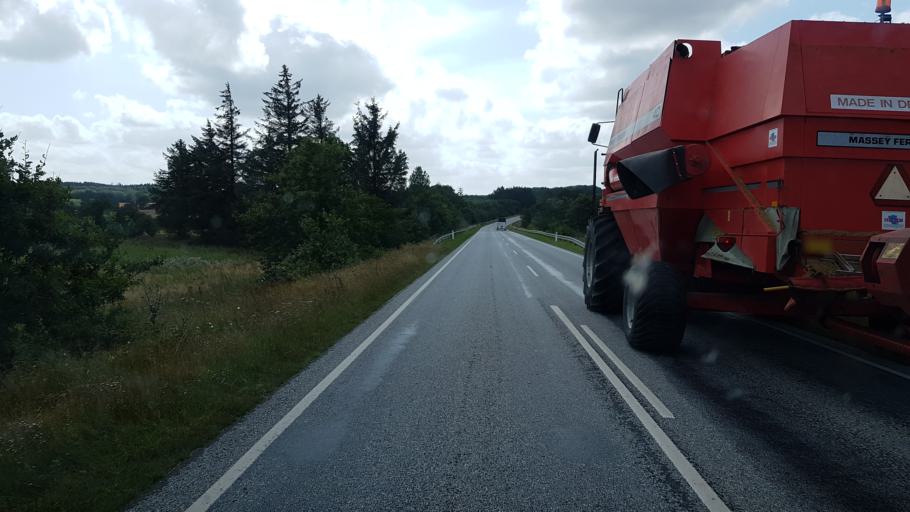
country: DK
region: South Denmark
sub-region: Vejen Kommune
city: Vejen
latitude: 55.5519
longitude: 9.1078
